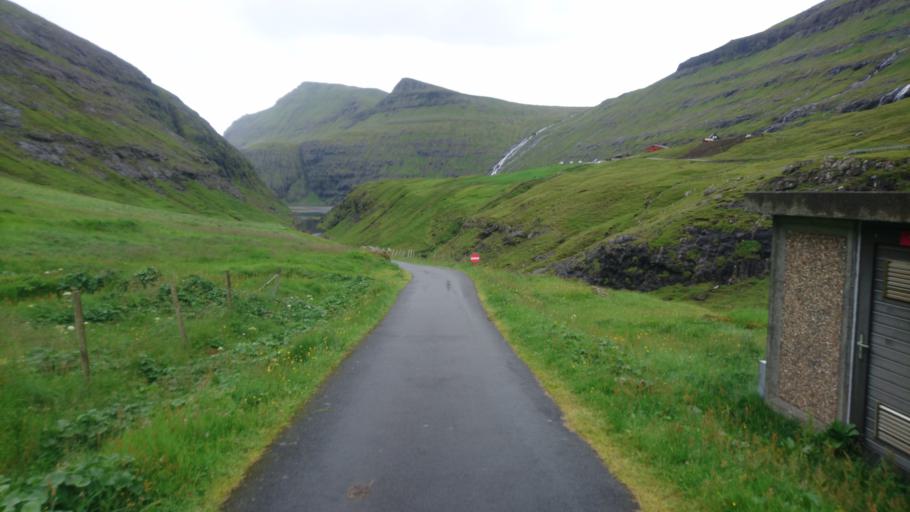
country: FO
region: Streymoy
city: Vestmanna
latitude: 62.2432
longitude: -7.1723
